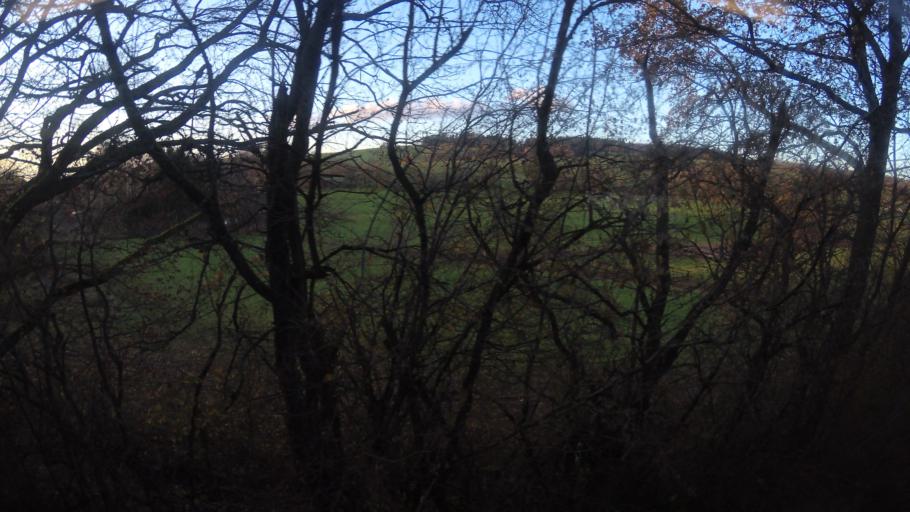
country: DE
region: Saarland
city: Hangard
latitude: 49.4184
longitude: 7.2007
